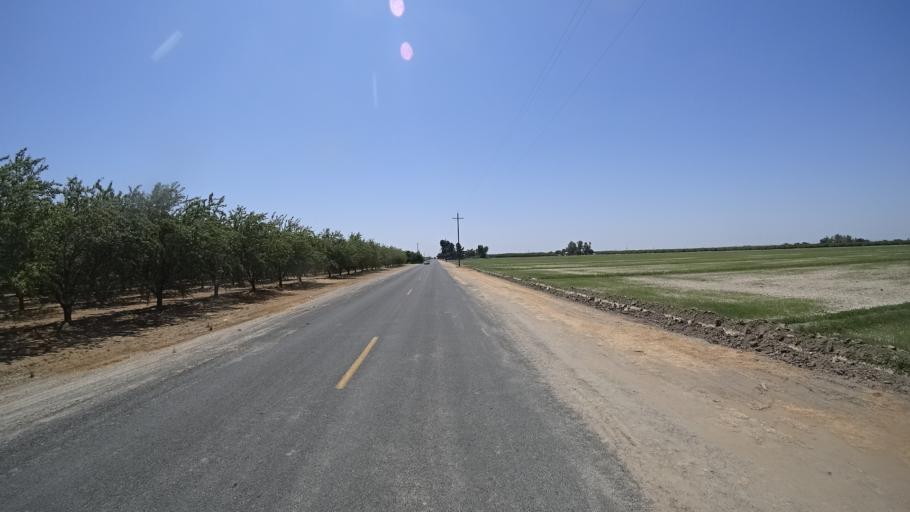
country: US
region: California
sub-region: Kings County
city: Armona
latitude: 36.2743
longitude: -119.7270
